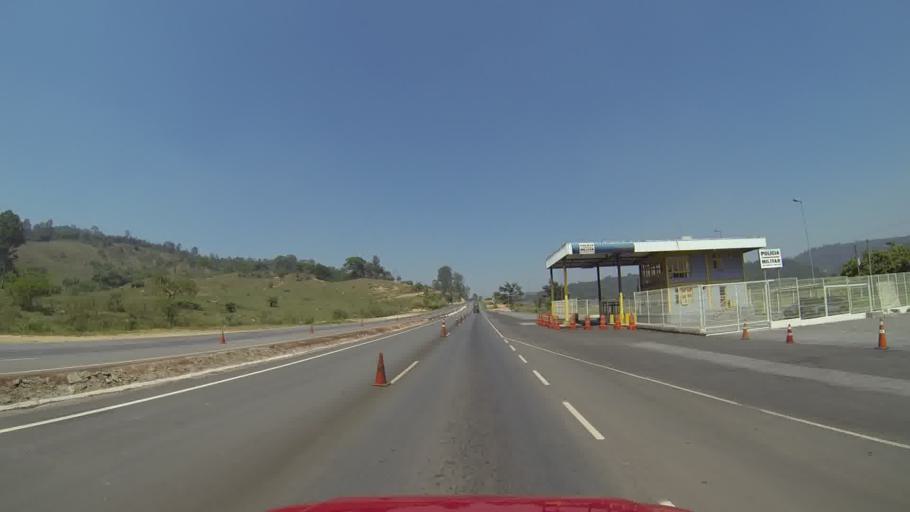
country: BR
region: Minas Gerais
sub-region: Mateus Leme
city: Mateus Leme
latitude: -20.0181
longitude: -44.4938
